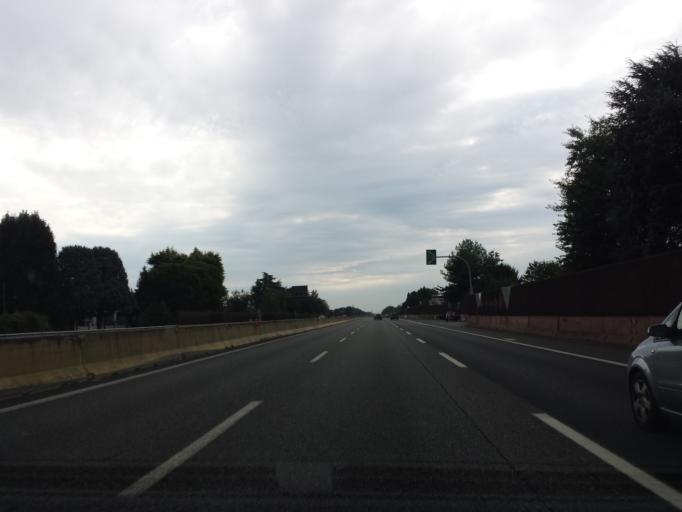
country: IT
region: Lombardy
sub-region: Citta metropolitana di Milano
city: Cerro Maggiore
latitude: 45.6003
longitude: 8.9516
